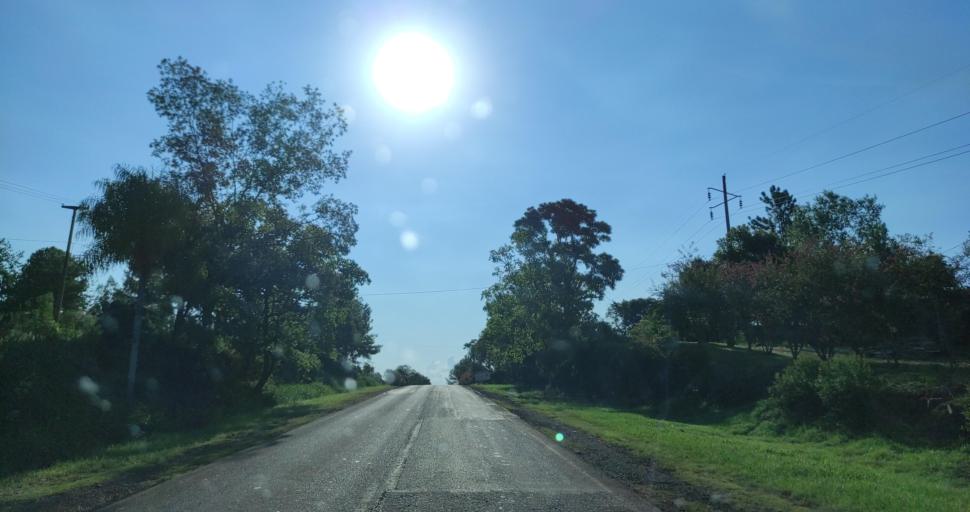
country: AR
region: Misiones
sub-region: Departamento de Eldorado
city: Eldorado
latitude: -26.4001
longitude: -54.4077
